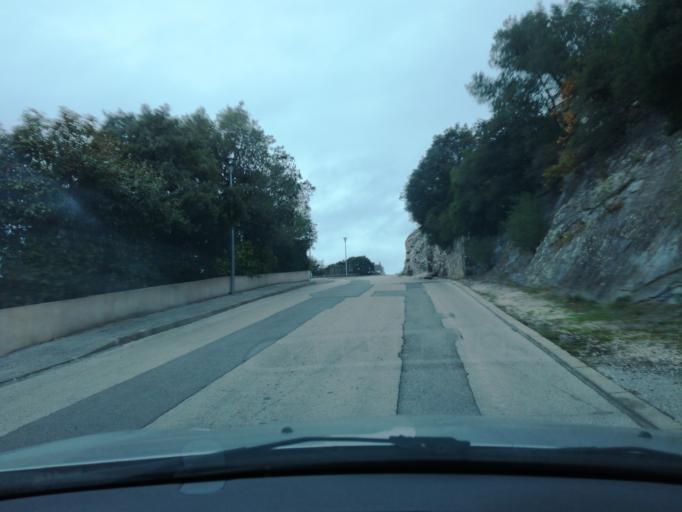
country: FR
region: Provence-Alpes-Cote d'Azur
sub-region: Departement du Var
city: Hyeres
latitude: 43.1243
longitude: 6.1229
